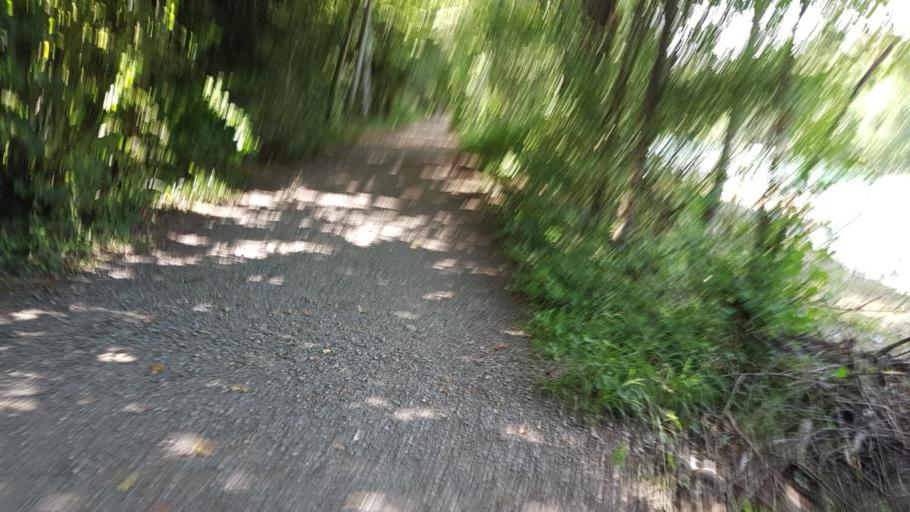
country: CH
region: Bern
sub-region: Bern-Mittelland District
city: Rubigen
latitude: 46.8957
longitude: 7.5312
